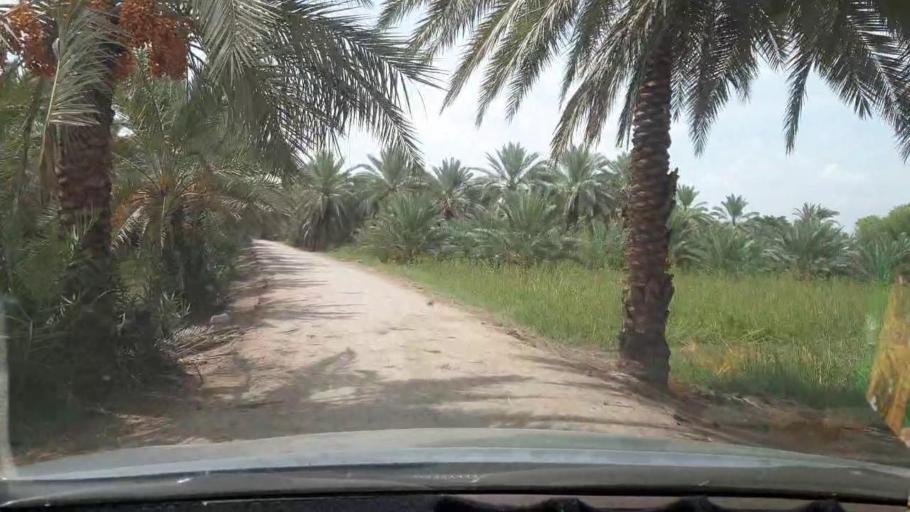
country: PK
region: Sindh
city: Khairpur
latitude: 27.4604
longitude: 68.8221
